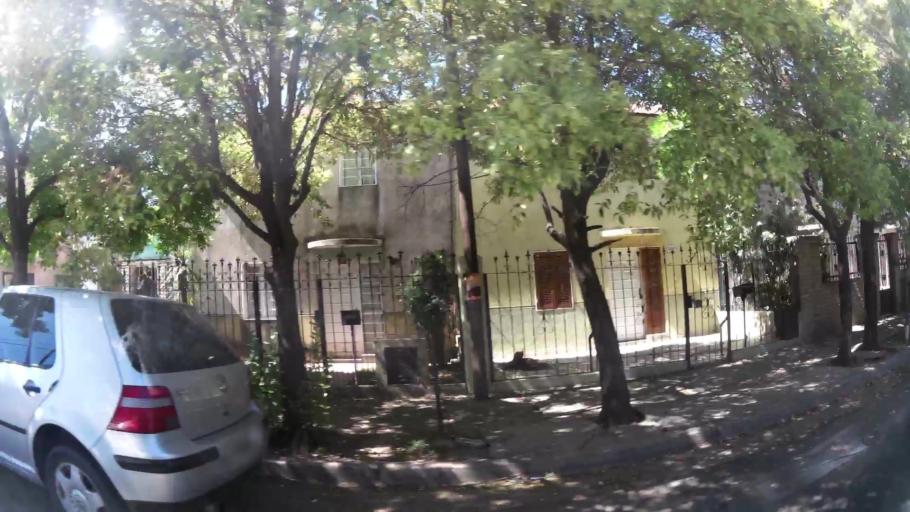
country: AR
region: Cordoba
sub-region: Departamento de Capital
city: Cordoba
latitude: -31.3759
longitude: -64.1567
